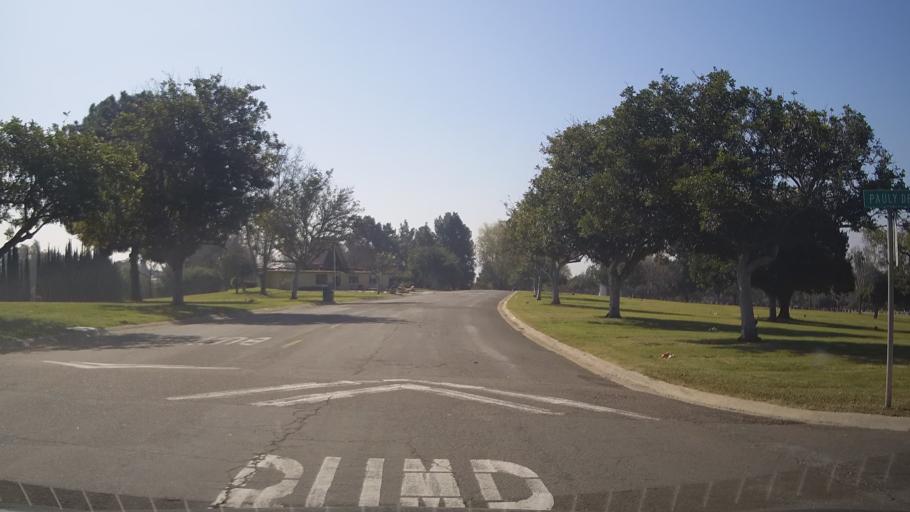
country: US
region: California
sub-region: San Diego County
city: National City
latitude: 32.7106
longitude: -117.1124
